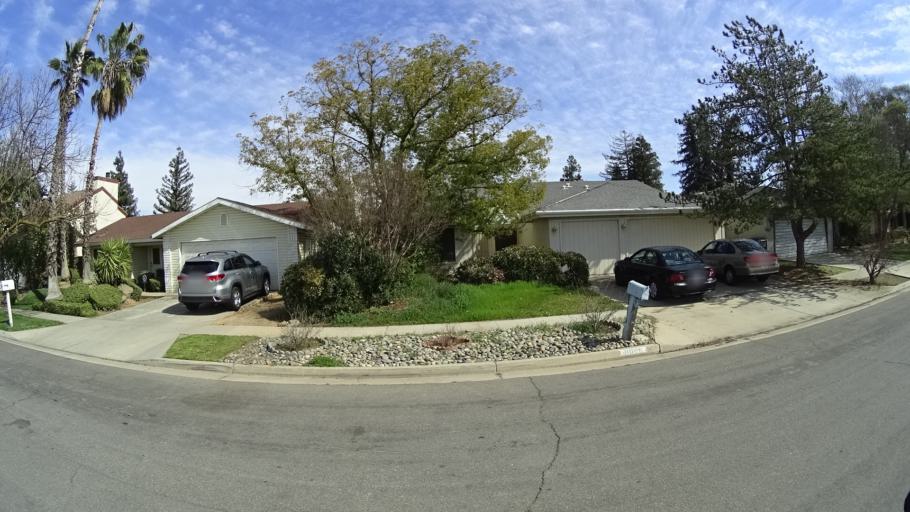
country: US
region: California
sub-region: Fresno County
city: Clovis
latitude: 36.8535
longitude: -119.7815
